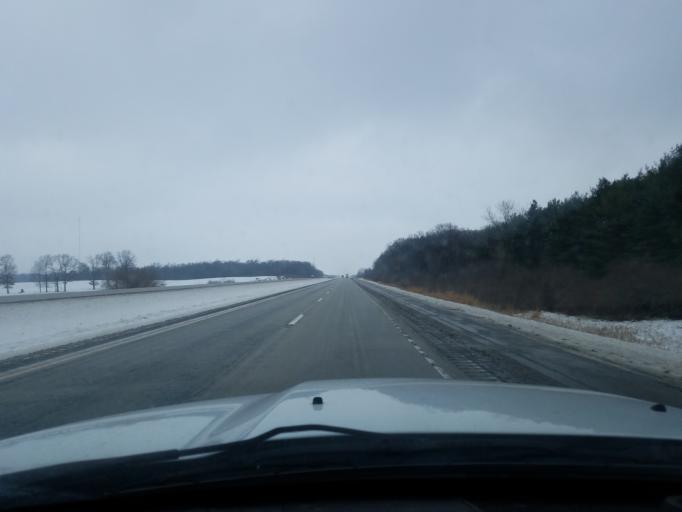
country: US
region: Indiana
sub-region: Fulton County
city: Rochester
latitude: 41.1248
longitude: -86.2395
